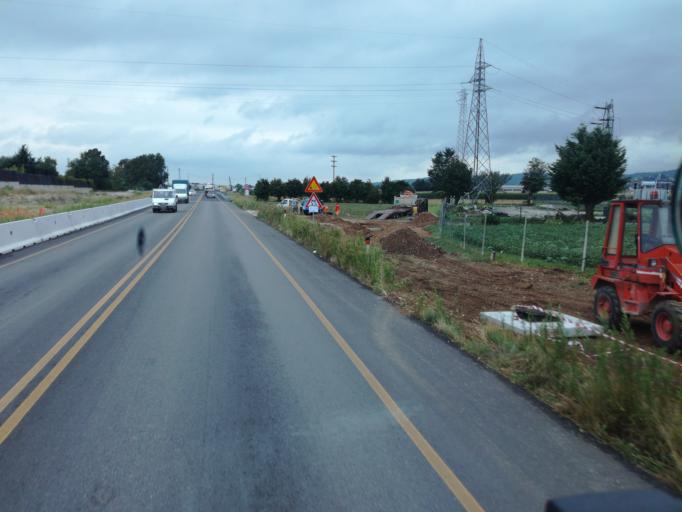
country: IT
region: Veneto
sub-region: Provincia di Vicenza
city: Nove
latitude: 45.7290
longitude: 11.6638
